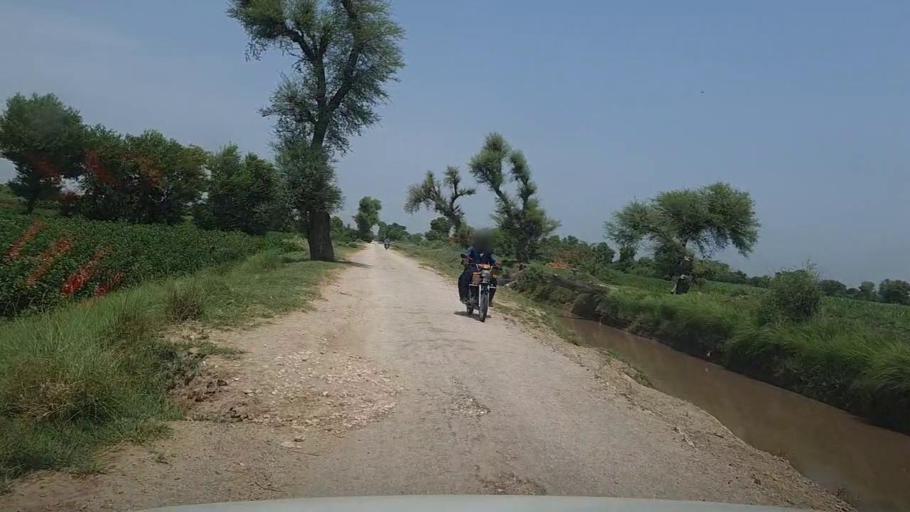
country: PK
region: Sindh
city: Karaundi
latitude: 26.8902
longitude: 68.3332
